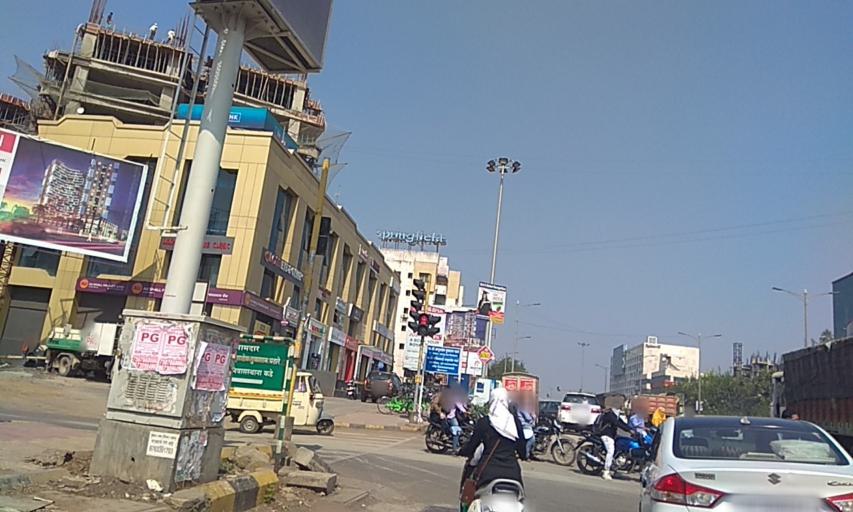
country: IN
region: Maharashtra
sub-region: Pune Division
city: Lohogaon
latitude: 18.5508
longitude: 73.9370
